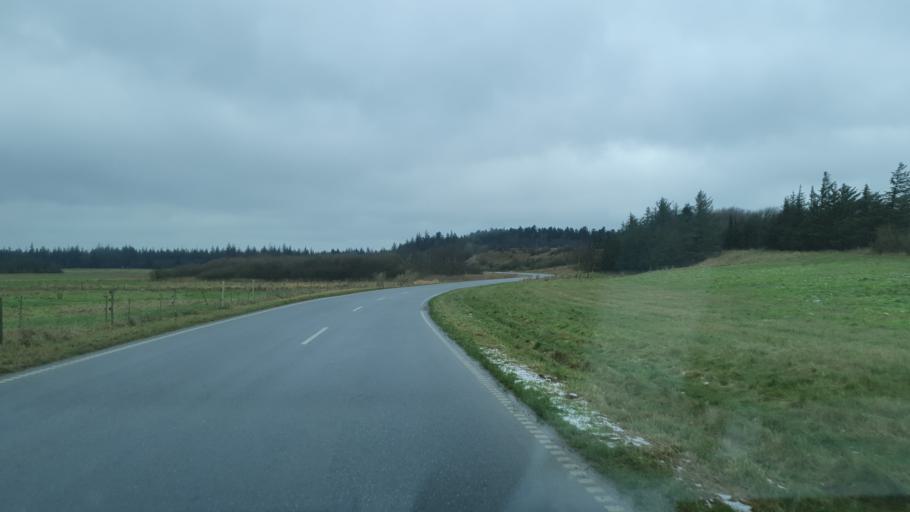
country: DK
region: North Denmark
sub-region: Jammerbugt Kommune
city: Fjerritslev
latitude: 57.1122
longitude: 9.1280
